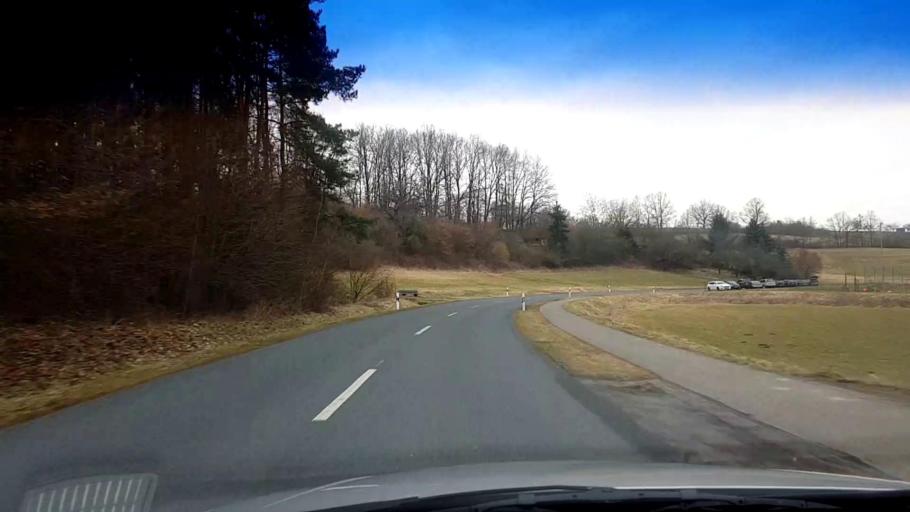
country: DE
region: Bavaria
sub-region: Upper Franconia
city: Bischberg
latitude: 49.9055
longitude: 10.8148
